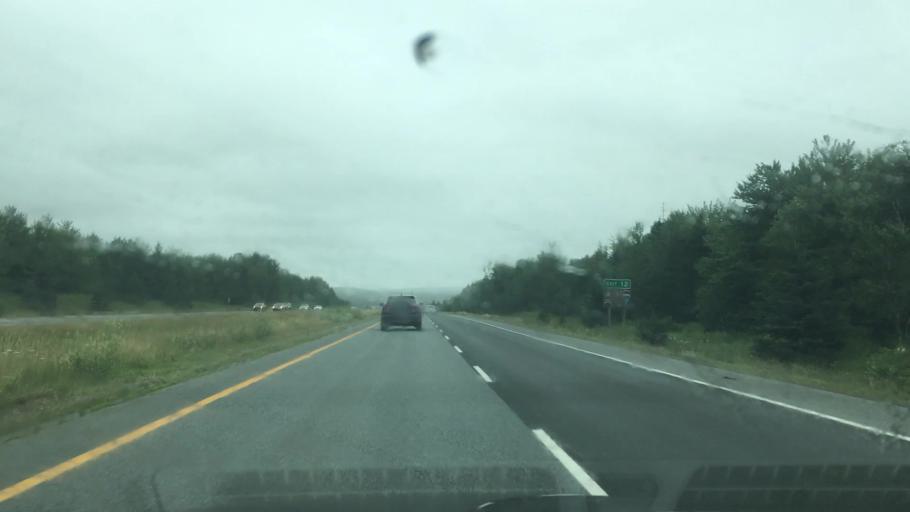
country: CA
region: Nova Scotia
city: Truro
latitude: 45.2383
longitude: -63.2938
